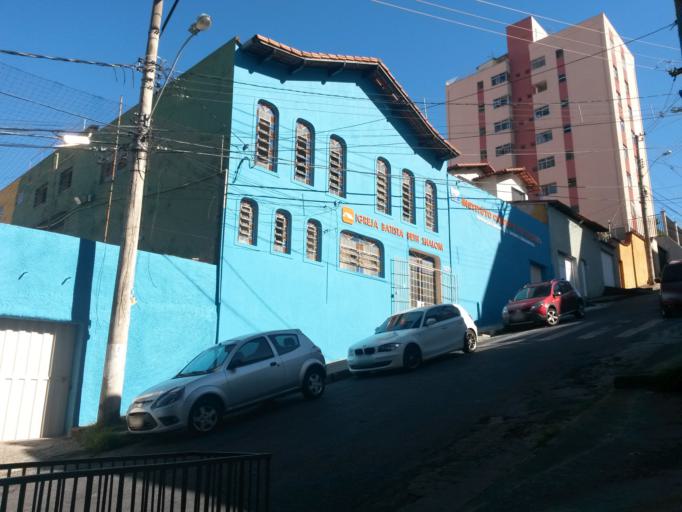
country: BR
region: Minas Gerais
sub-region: Belo Horizonte
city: Belo Horizonte
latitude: -19.9112
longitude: -43.9775
